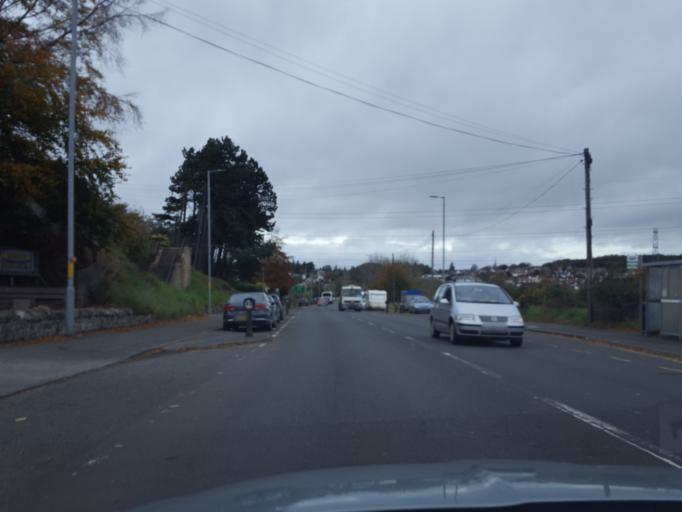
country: GB
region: Scotland
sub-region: Midlothian
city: Loanhead
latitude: 55.8919
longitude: -3.2013
